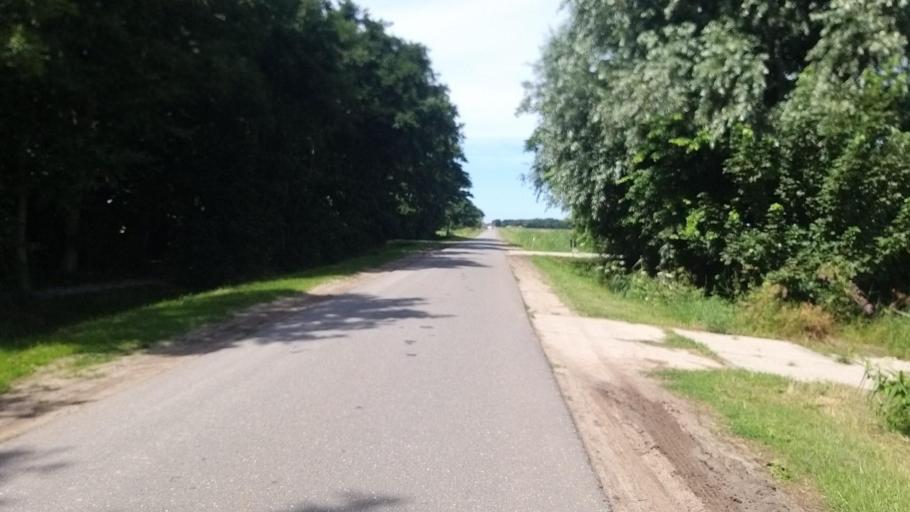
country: NL
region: North Holland
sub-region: Gemeente Texel
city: Den Burg
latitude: 53.1417
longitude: 4.8736
